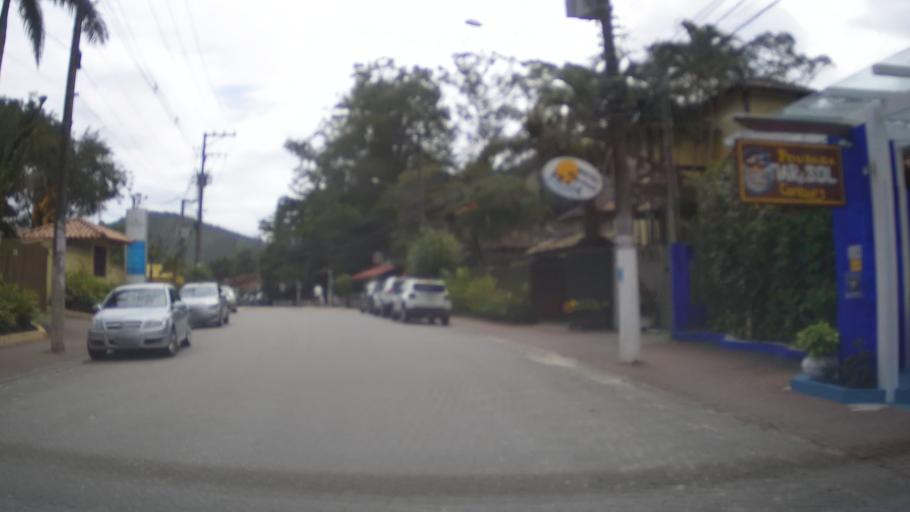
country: BR
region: Sao Paulo
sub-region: Sao Sebastiao
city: Sao Sebastiao
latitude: -23.7754
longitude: -45.6487
